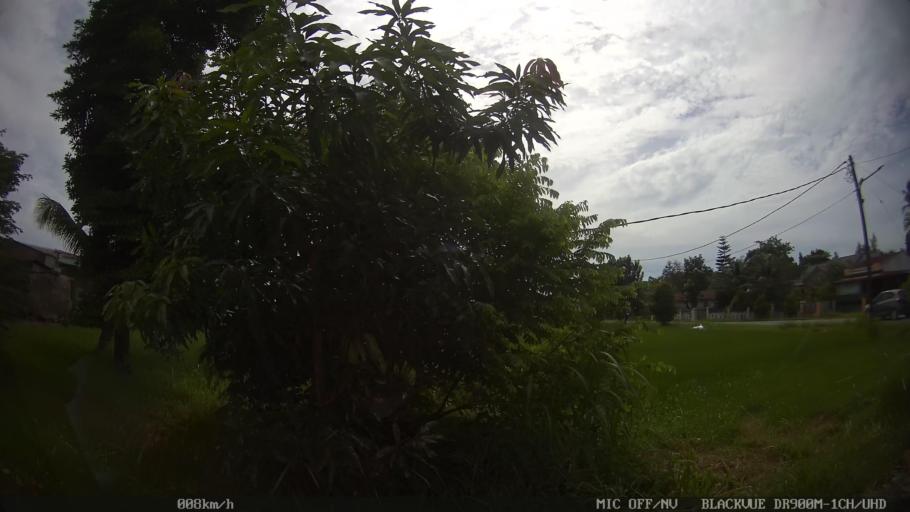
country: ID
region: North Sumatra
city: Percut
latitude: 3.6198
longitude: 98.7911
